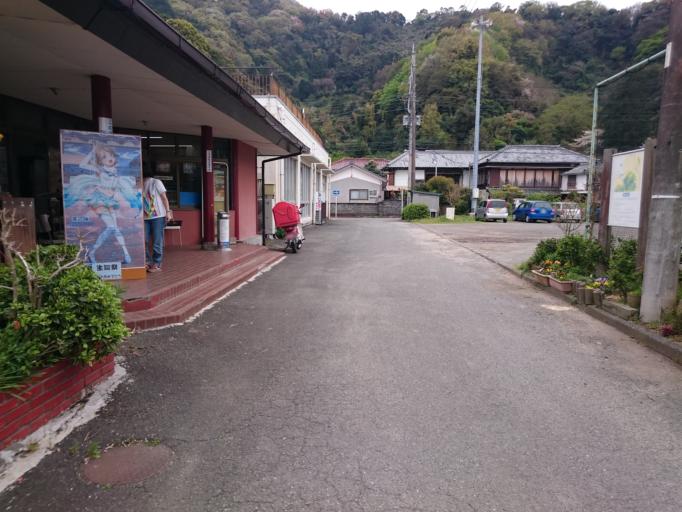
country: JP
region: Shizuoka
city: Numazu
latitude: 35.0177
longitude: 138.8933
